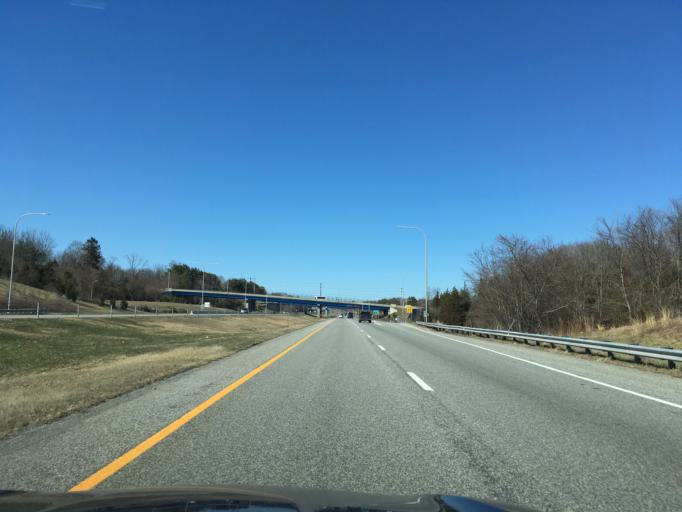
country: US
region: Rhode Island
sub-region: Kent County
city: East Greenwich
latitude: 41.6251
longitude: -71.4867
